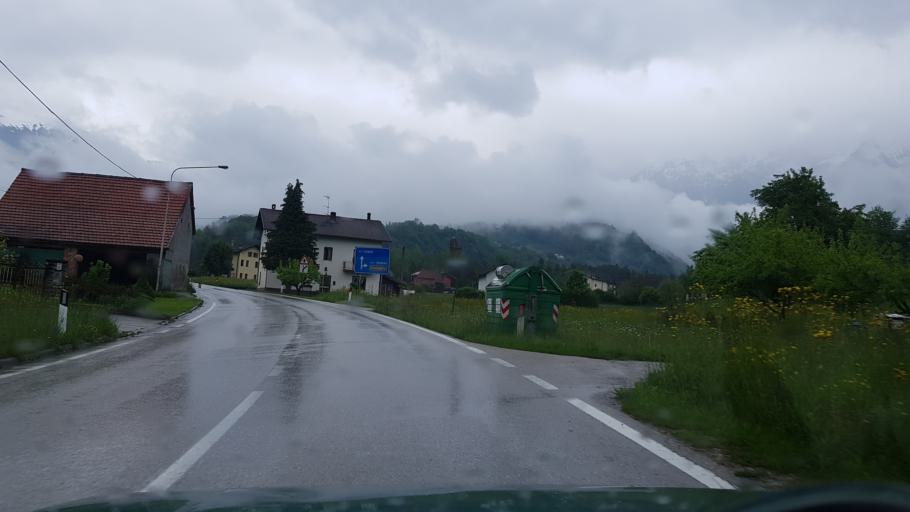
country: IT
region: Veneto
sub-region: Provincia di Belluno
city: Puos d'Alpago
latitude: 46.1460
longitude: 12.3838
